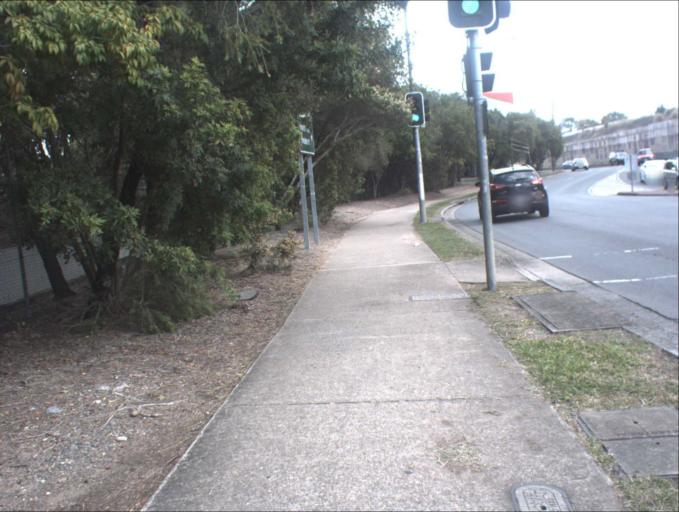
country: AU
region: Queensland
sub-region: Brisbane
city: Sunnybank Hills
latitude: -27.6645
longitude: 153.0357
